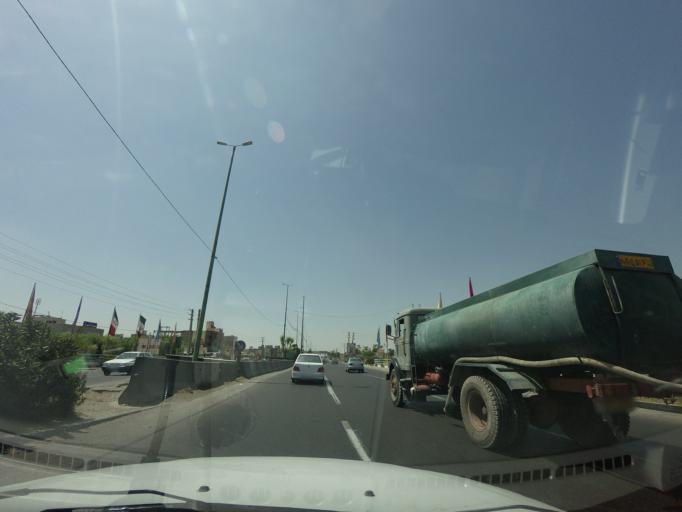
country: IR
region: Tehran
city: Eslamshahr
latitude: 35.5902
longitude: 51.2896
